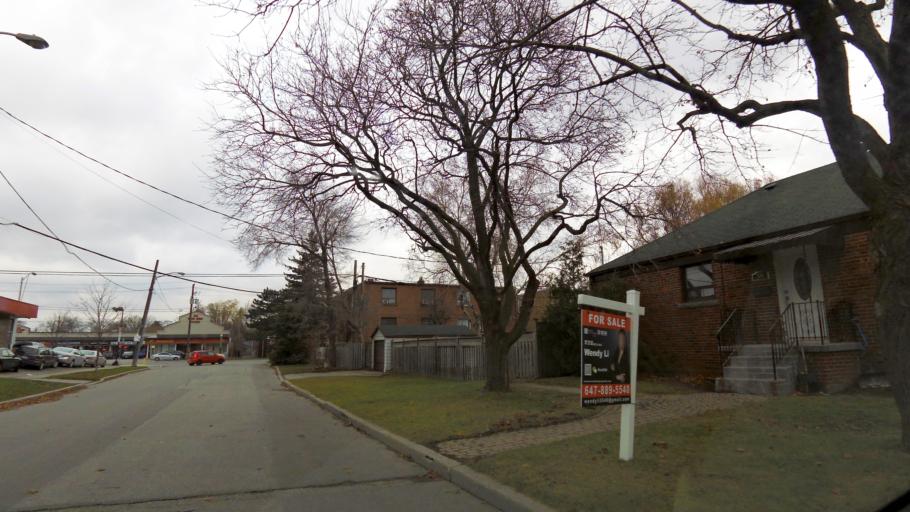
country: CA
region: Ontario
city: North York
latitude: 43.7350
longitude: -79.4416
